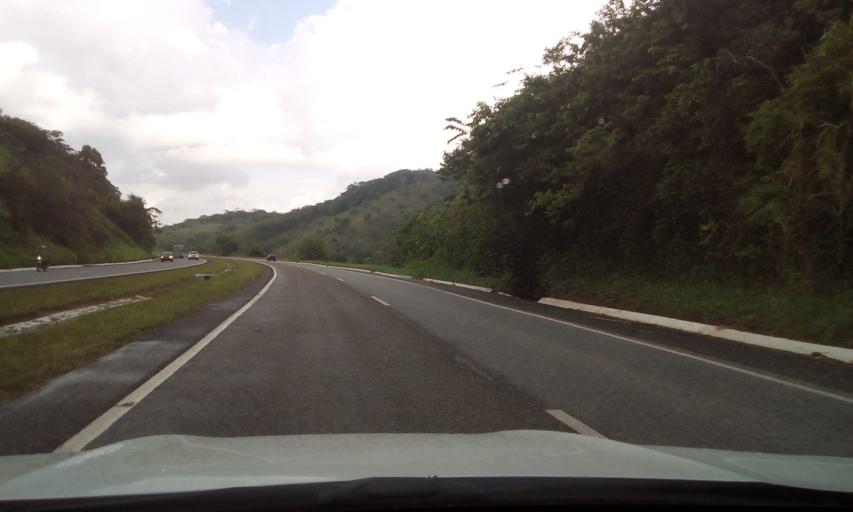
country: BR
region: Pernambuco
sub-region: Cabo De Santo Agostinho
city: Cabo
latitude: -8.2660
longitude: -35.0518
